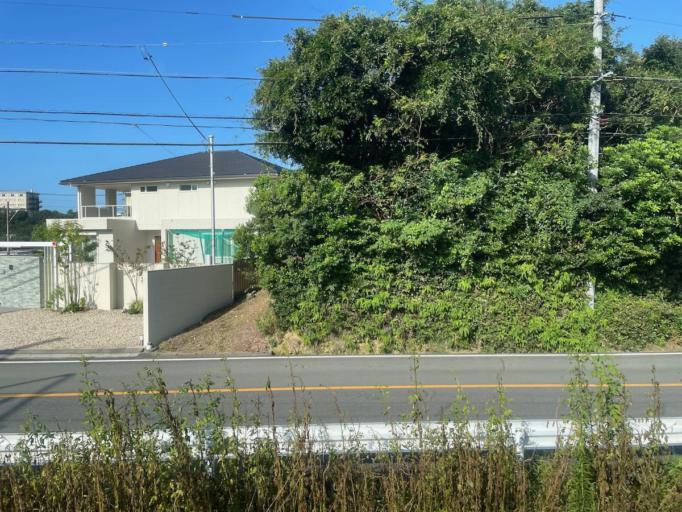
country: JP
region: Mie
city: Toba
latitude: 34.3126
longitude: 136.8253
